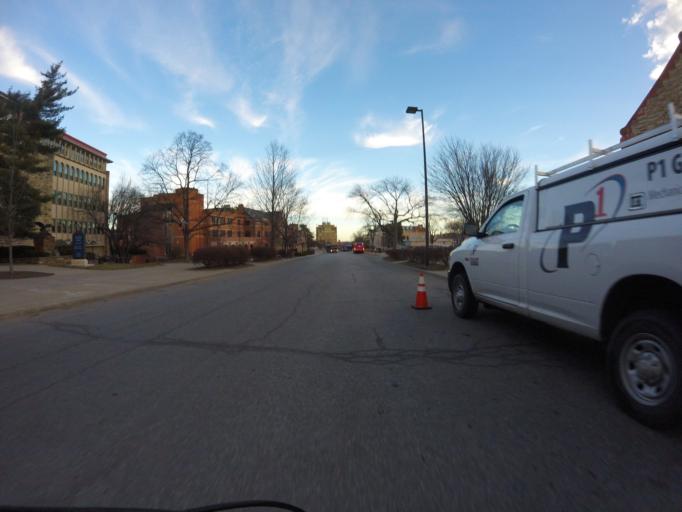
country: US
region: Kansas
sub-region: Douglas County
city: Lawrence
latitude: 38.9527
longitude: -95.2607
